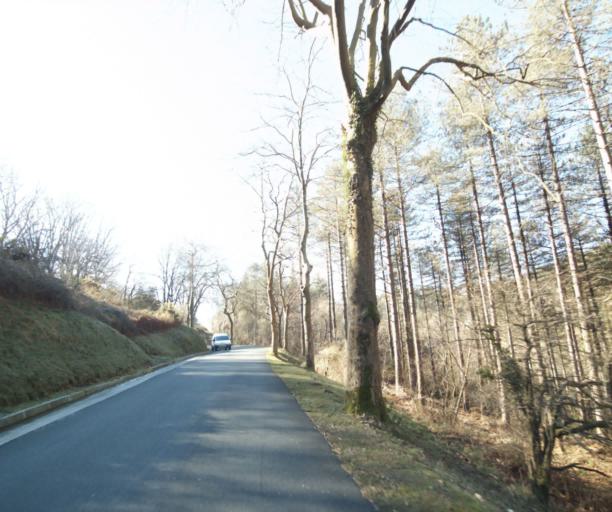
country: ES
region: Navarre
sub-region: Provincia de Navarra
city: Bera
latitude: 43.3141
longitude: -1.6849
